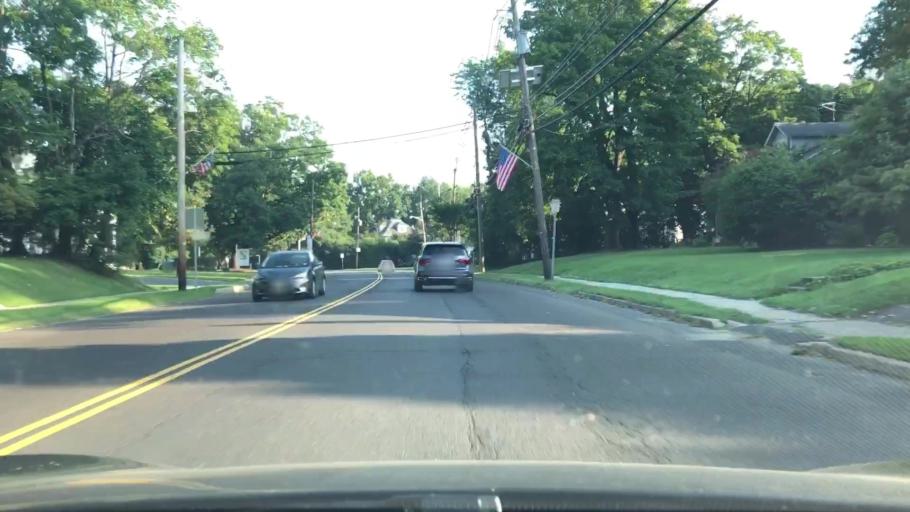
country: US
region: New Jersey
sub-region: Mercer County
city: Pennington
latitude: 40.3181
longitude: -74.7901
